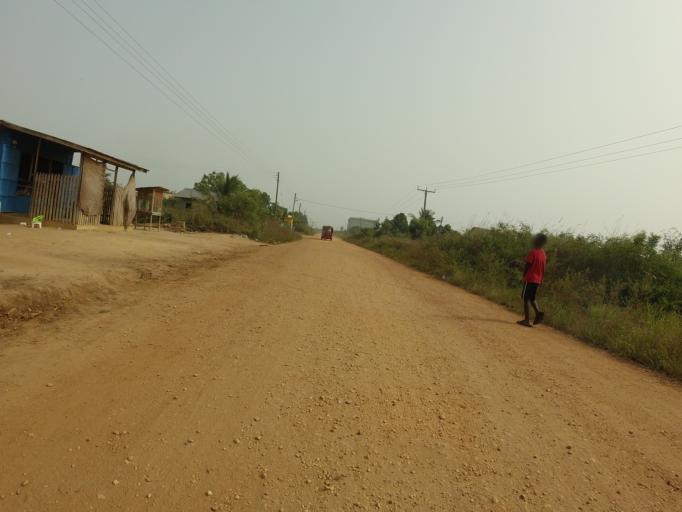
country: GH
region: Volta
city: Anloga
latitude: 5.9875
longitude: 0.5983
